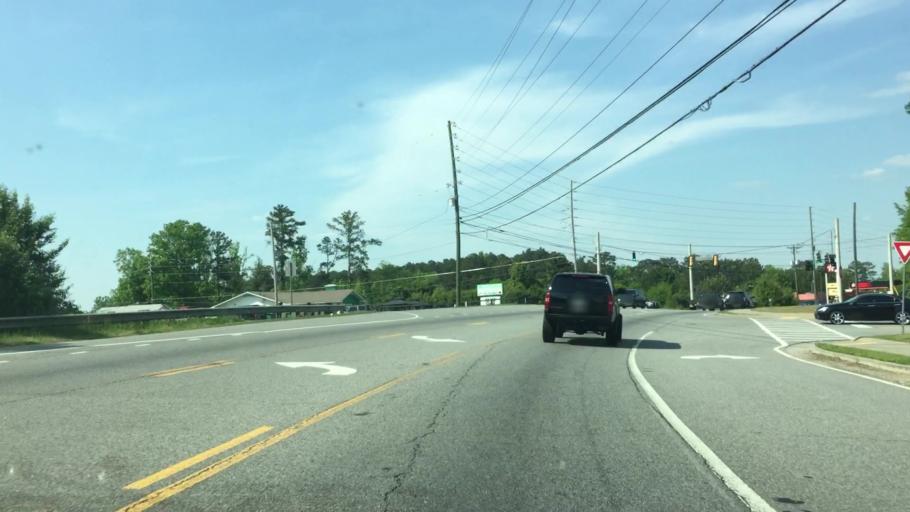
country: US
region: Georgia
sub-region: Fulton County
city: Milton
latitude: 34.1524
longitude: -84.2519
